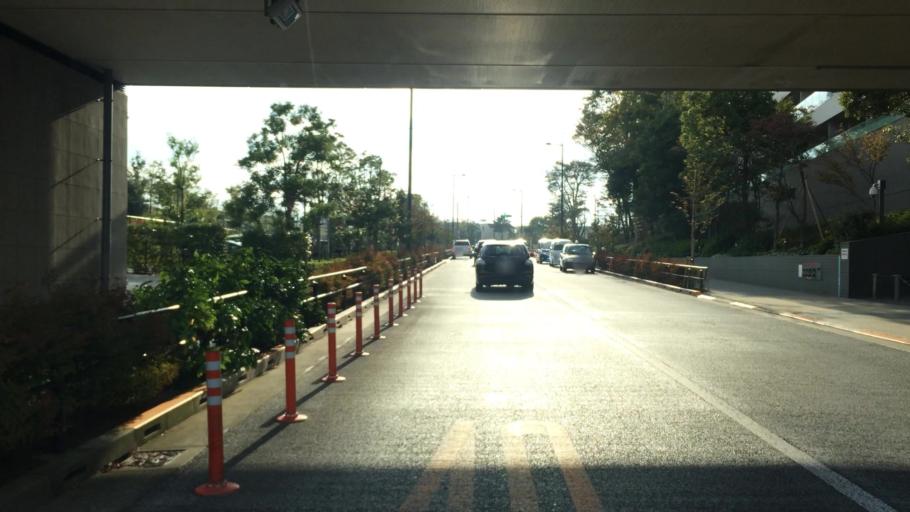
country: JP
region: Tokyo
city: Chofugaoka
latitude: 35.6094
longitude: 139.6327
